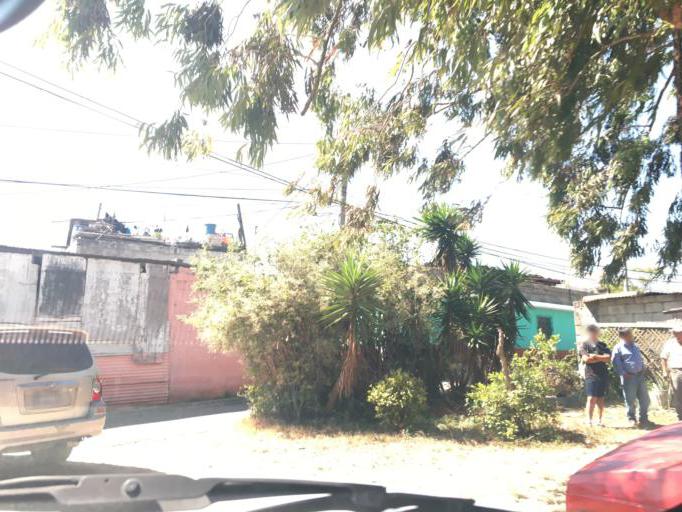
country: GT
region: Guatemala
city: Mixco
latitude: 14.6219
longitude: -90.5827
